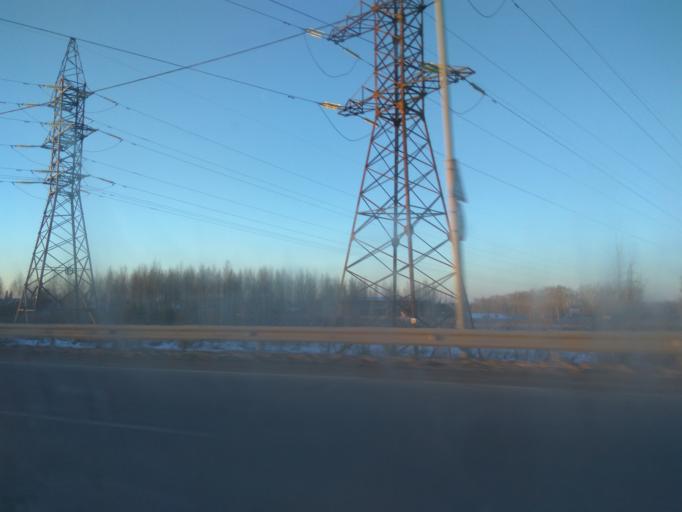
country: RU
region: Novosibirsk
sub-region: Novosibirskiy Rayon
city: Novosibirsk
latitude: 55.1342
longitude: 82.9783
